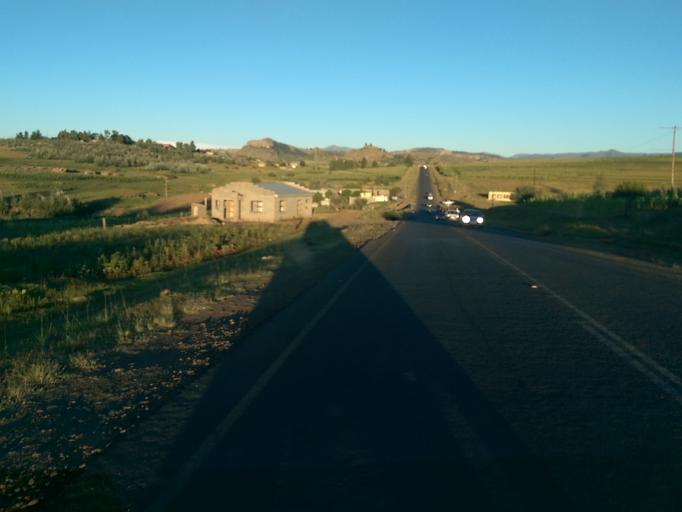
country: LS
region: Maseru
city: Maseru
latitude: -29.4084
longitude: 27.5947
